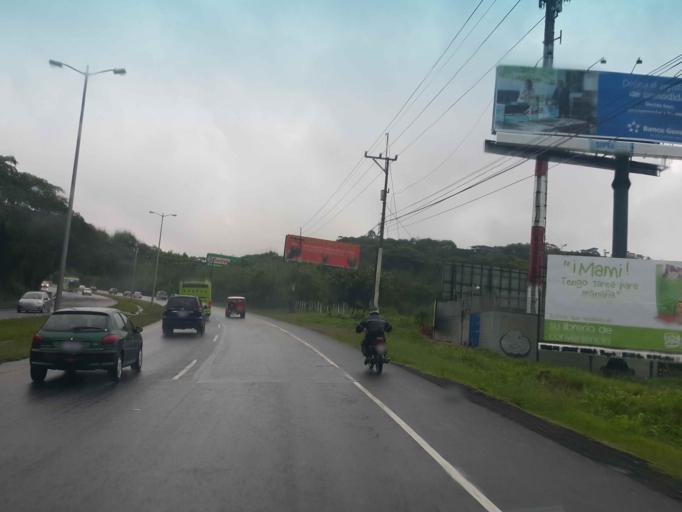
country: CR
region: San Jose
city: Santa Ana
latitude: 9.9434
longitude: -84.1705
